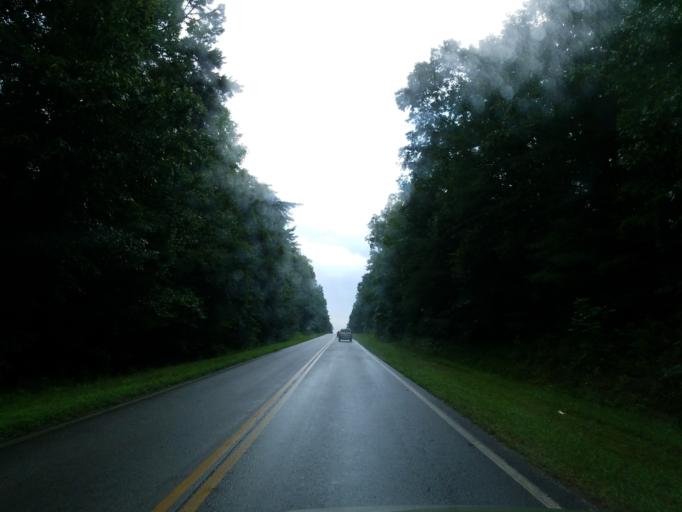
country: US
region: Georgia
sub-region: Lumpkin County
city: Dahlonega
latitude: 34.5360
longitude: -83.8950
